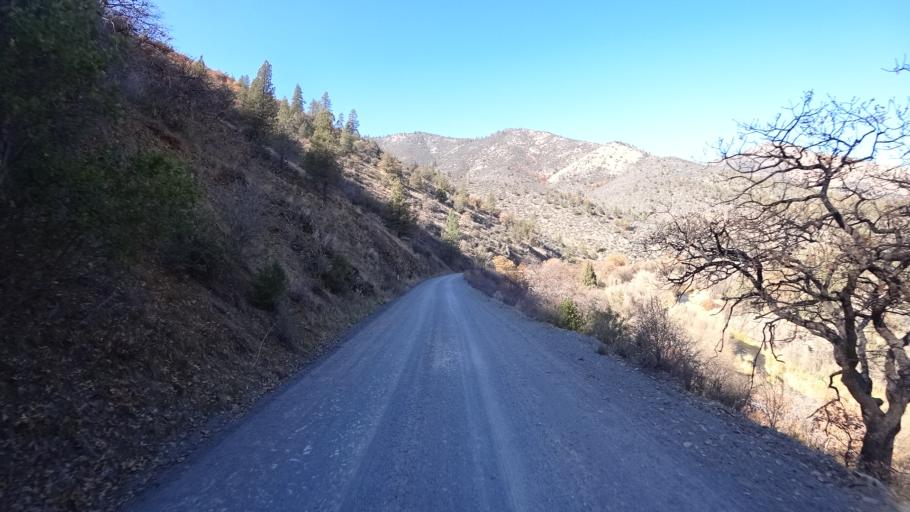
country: US
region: California
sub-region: Siskiyou County
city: Yreka
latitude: 41.7907
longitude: -122.6092
